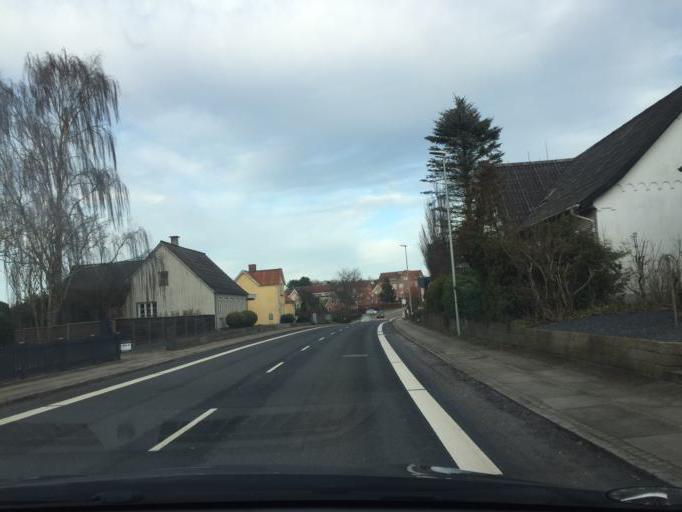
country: DK
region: South Denmark
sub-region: Faaborg-Midtfyn Kommune
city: Ringe
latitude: 55.2323
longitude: 10.4709
